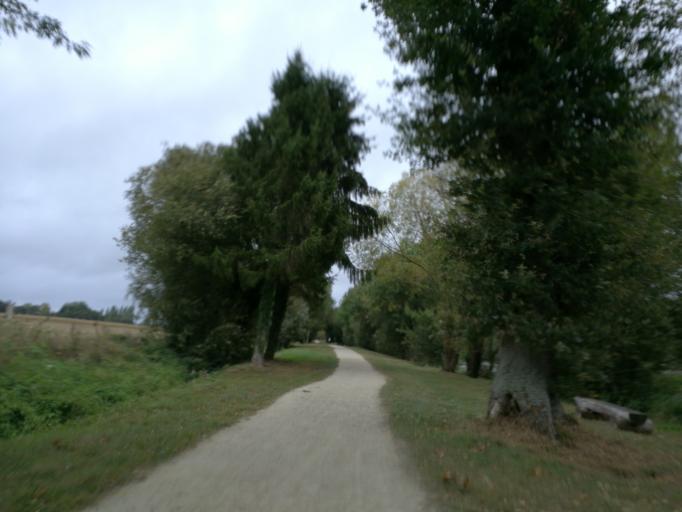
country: FR
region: Brittany
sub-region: Departement d'Ille-et-Vilaine
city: Bedee
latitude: 48.1677
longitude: -1.9551
